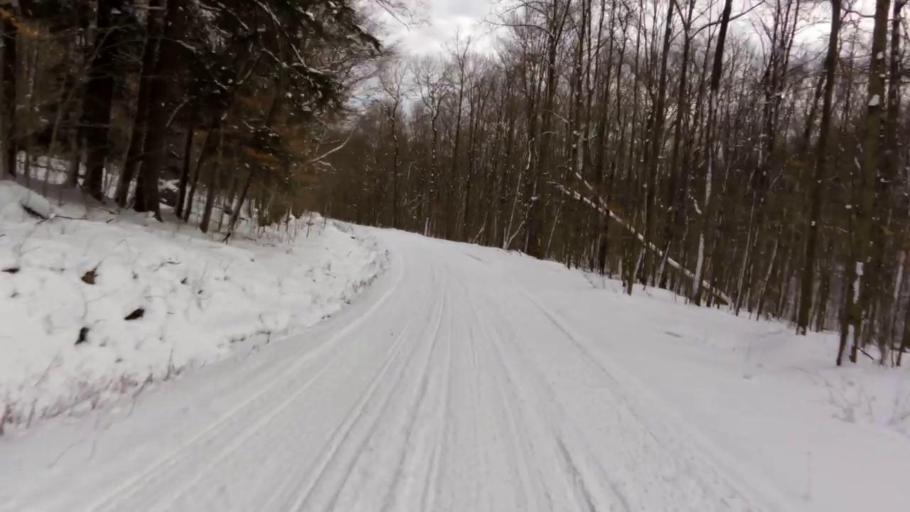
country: US
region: New York
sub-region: Cattaraugus County
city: Salamanca
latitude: 42.0537
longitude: -78.7604
